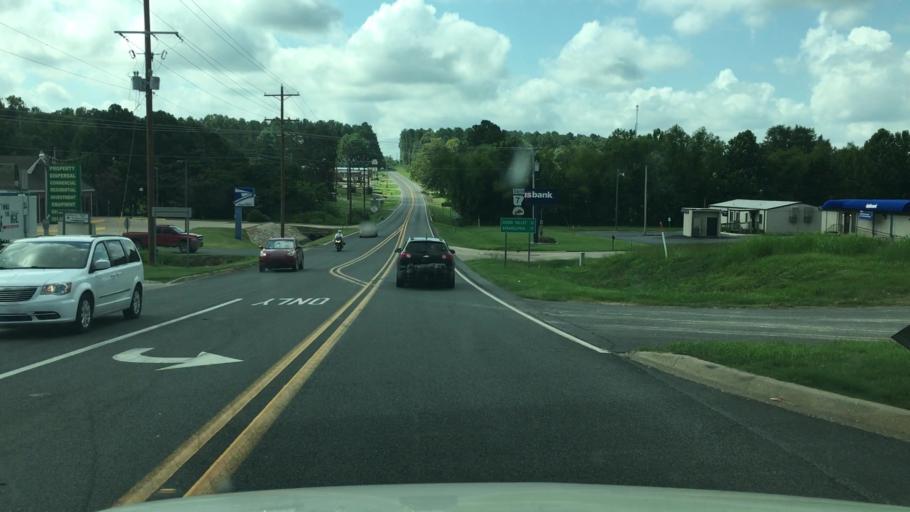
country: US
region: Arkansas
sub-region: Garland County
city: Lake Hamilton
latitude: 34.3162
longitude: -93.1709
